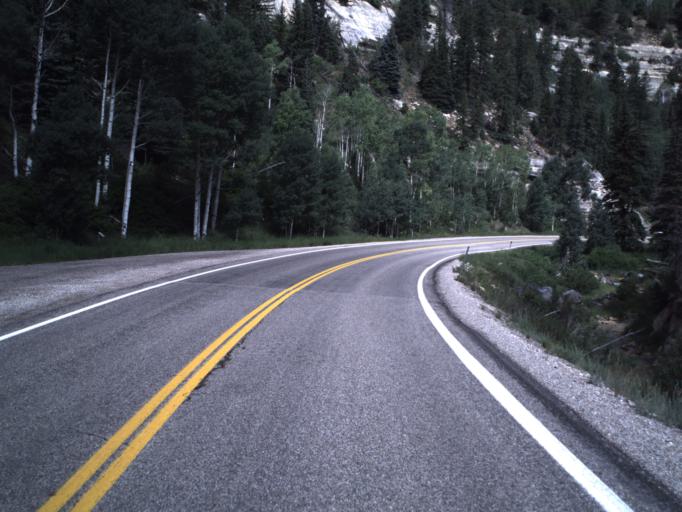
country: US
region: Utah
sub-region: Iron County
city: Cedar City
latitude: 37.6029
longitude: -112.9357
